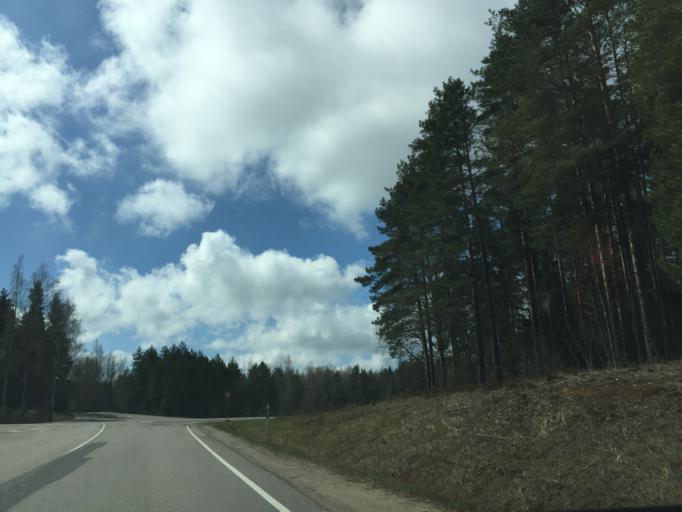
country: LV
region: Apes Novads
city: Ape
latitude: 57.5188
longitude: 26.7029
